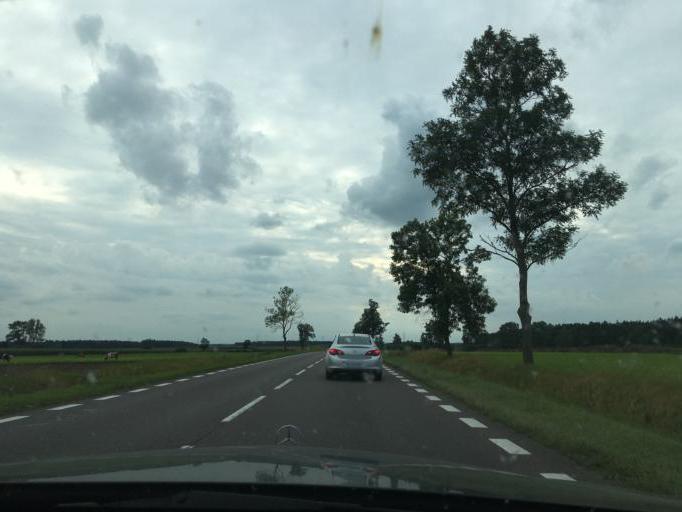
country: PL
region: Podlasie
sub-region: Powiat grajewski
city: Szczuczyn
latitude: 53.6059
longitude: 22.3689
